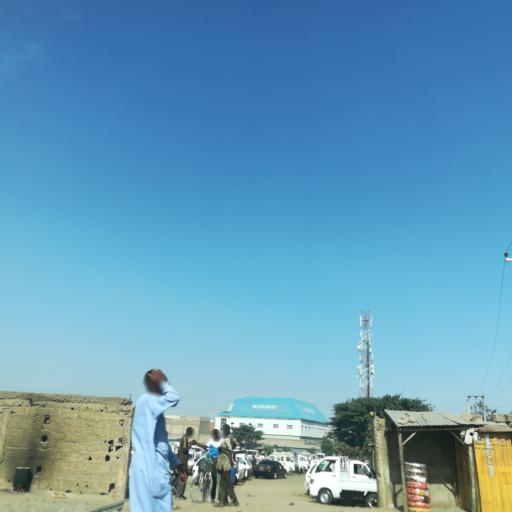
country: NG
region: Kano
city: Kano
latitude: 12.0107
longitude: 8.5226
